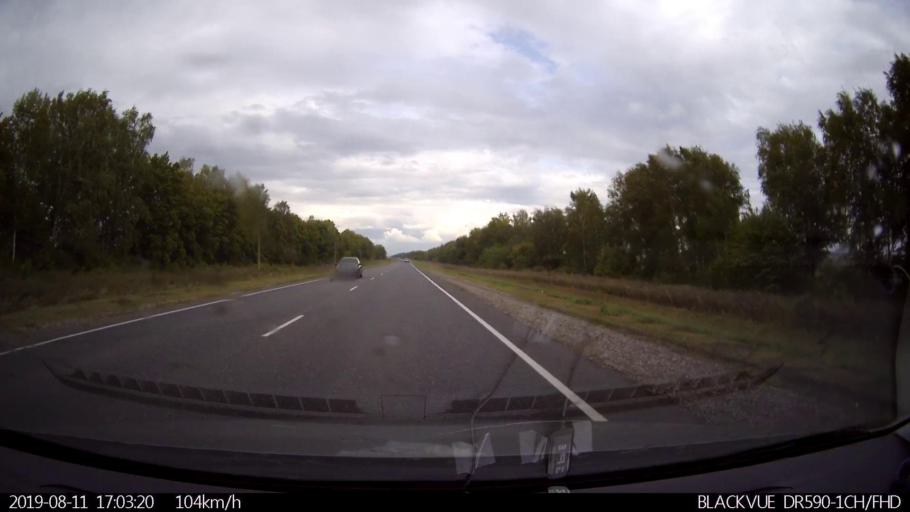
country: RU
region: Ulyanovsk
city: Mayna
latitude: 54.3033
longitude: 47.7375
